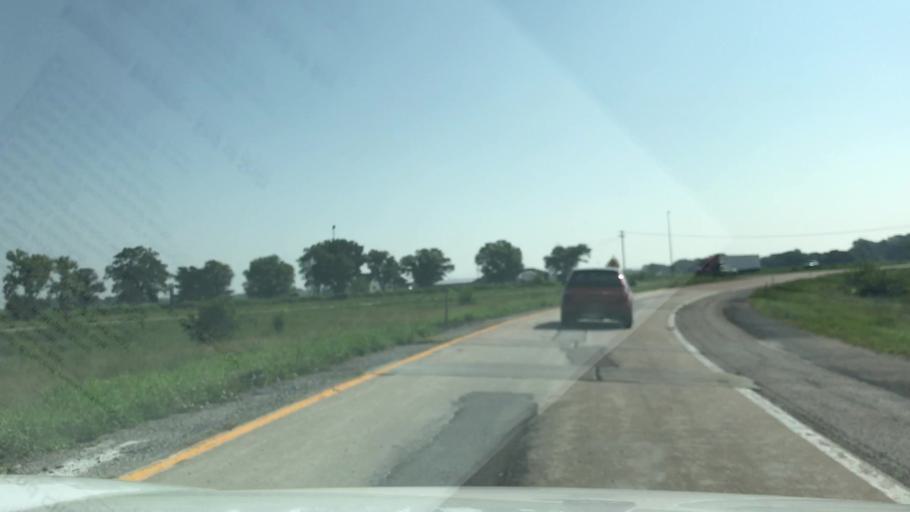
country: US
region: Illinois
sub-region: Saint Clair County
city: Scott Air Force Base
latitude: 38.5506
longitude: -89.8046
